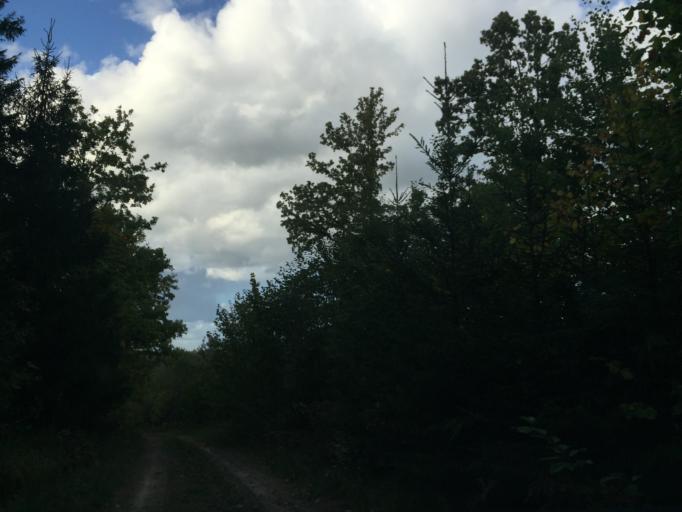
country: LV
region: Ligatne
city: Ligatne
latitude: 57.1180
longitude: 25.1358
